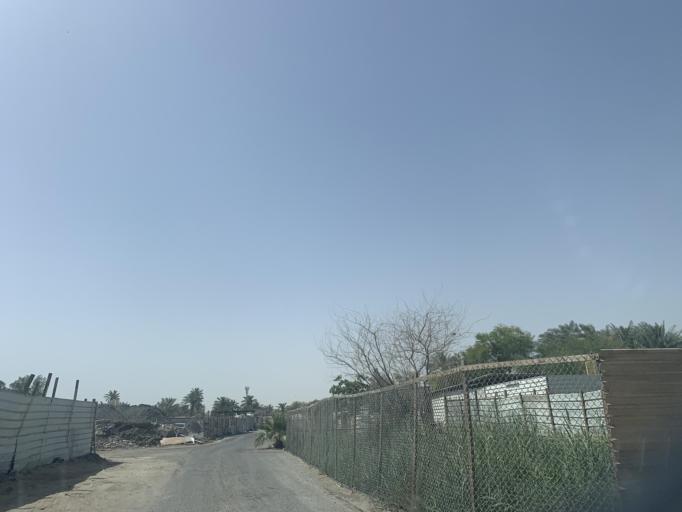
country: BH
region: Manama
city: Jidd Hafs
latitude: 26.2024
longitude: 50.5417
